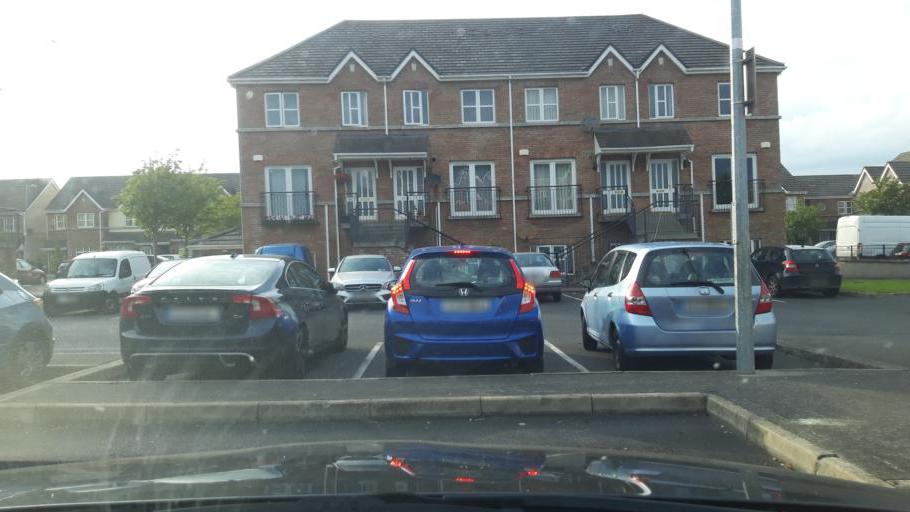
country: IE
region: Leinster
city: Hartstown
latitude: 53.3968
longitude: -6.4339
